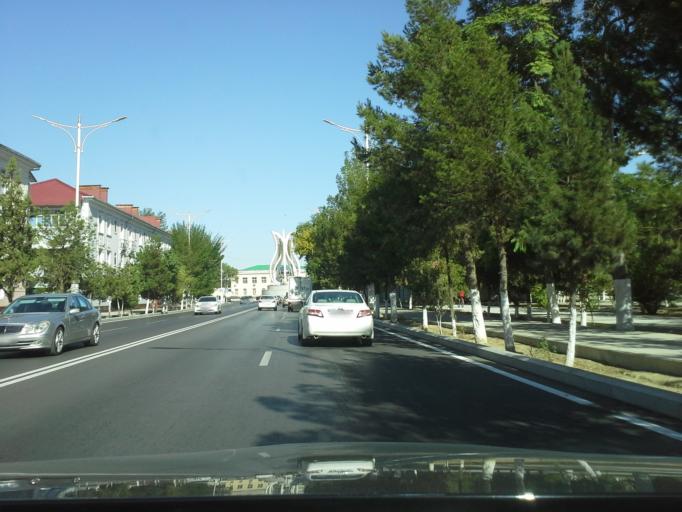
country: TM
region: Ahal
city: Ashgabat
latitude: 37.9578
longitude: 58.3564
